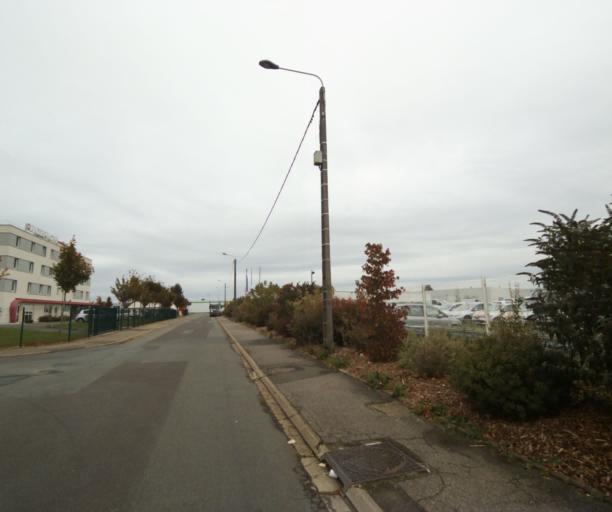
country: FR
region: Centre
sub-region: Departement d'Eure-et-Loir
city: Dreux
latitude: 48.7456
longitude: 1.3423
